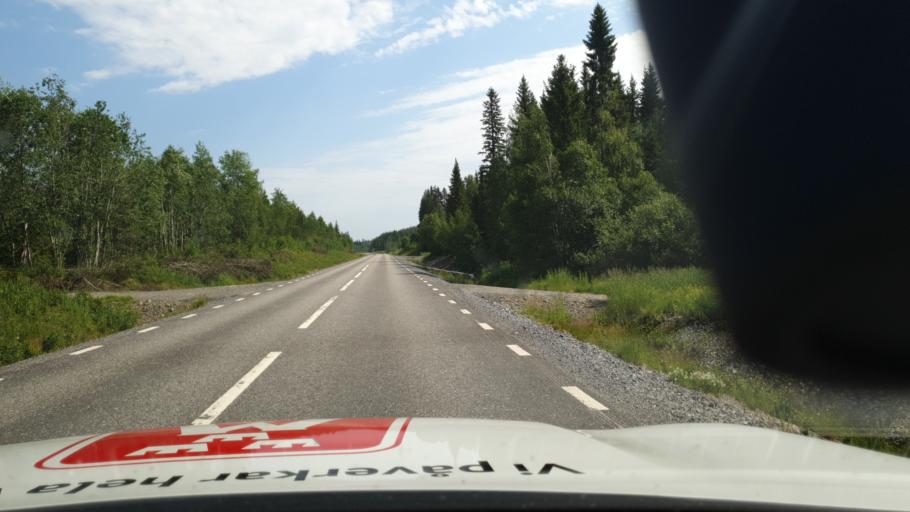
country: SE
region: Vaesterbotten
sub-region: Vindelns Kommun
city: Vindeln
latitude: 64.2548
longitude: 19.9390
